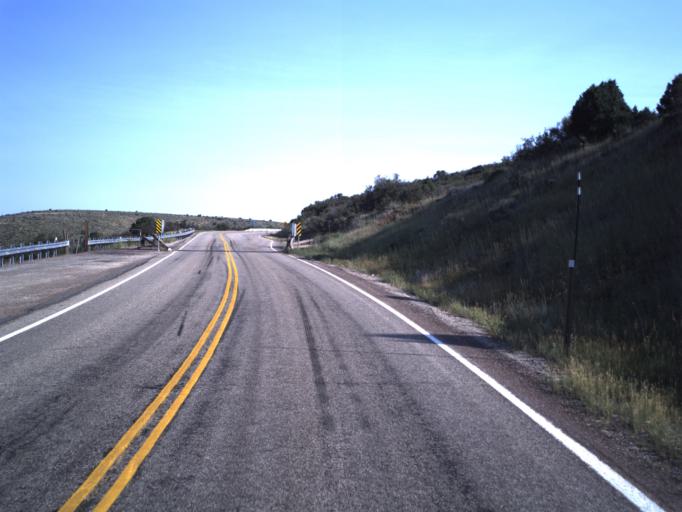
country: US
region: Utah
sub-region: Uintah County
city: Vernal
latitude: 40.6672
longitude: -109.4817
